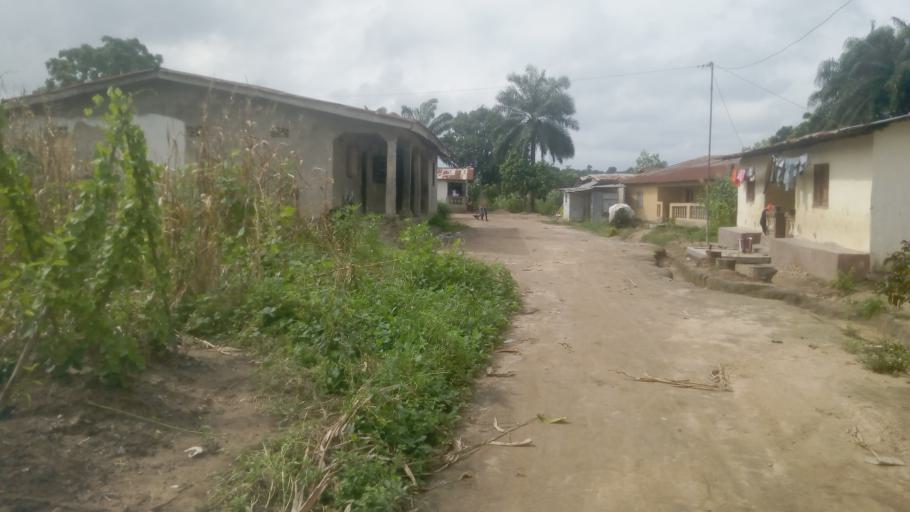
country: SL
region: Northern Province
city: Lunsar
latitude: 8.6944
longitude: -12.5364
